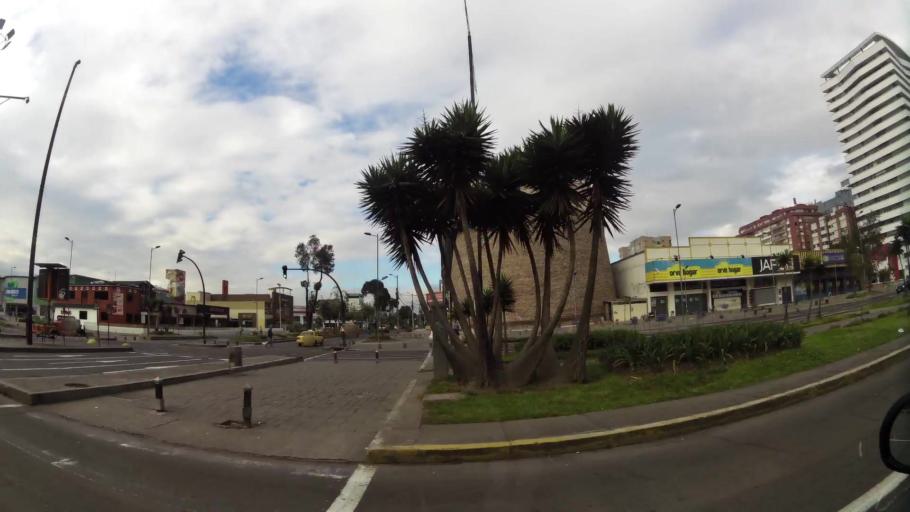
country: EC
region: Pichincha
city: Quito
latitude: -0.1757
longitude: -78.4857
